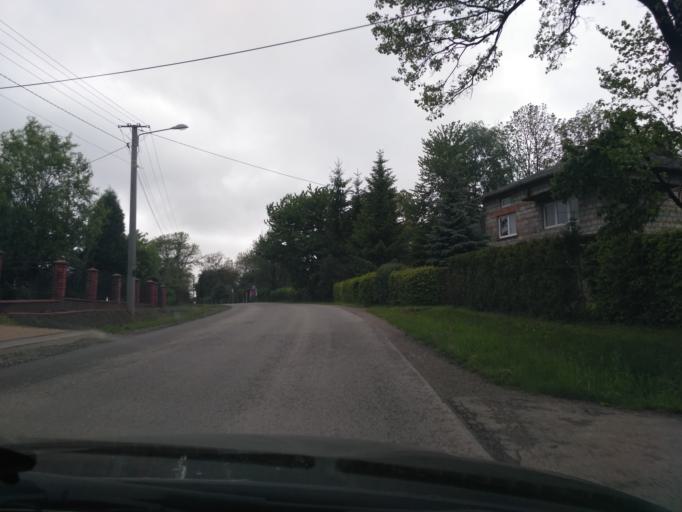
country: PL
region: Subcarpathian Voivodeship
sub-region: Powiat jasielski
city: Jaslo
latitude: 49.8025
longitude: 21.5168
